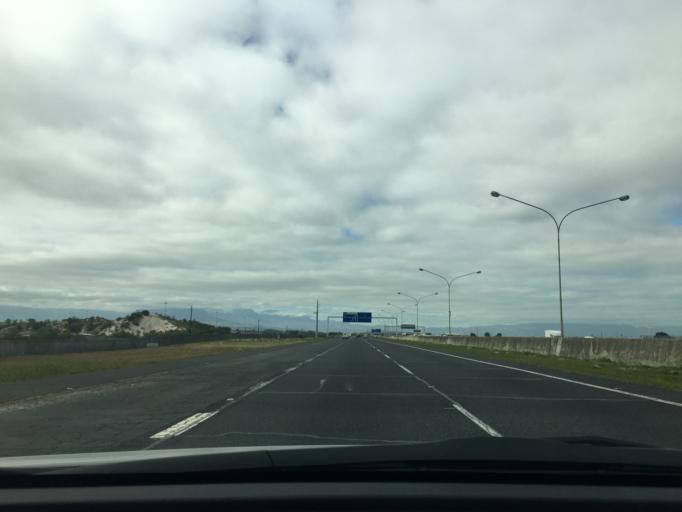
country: ZA
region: Western Cape
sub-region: City of Cape Town
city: Lansdowne
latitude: -34.0053
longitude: 18.6433
